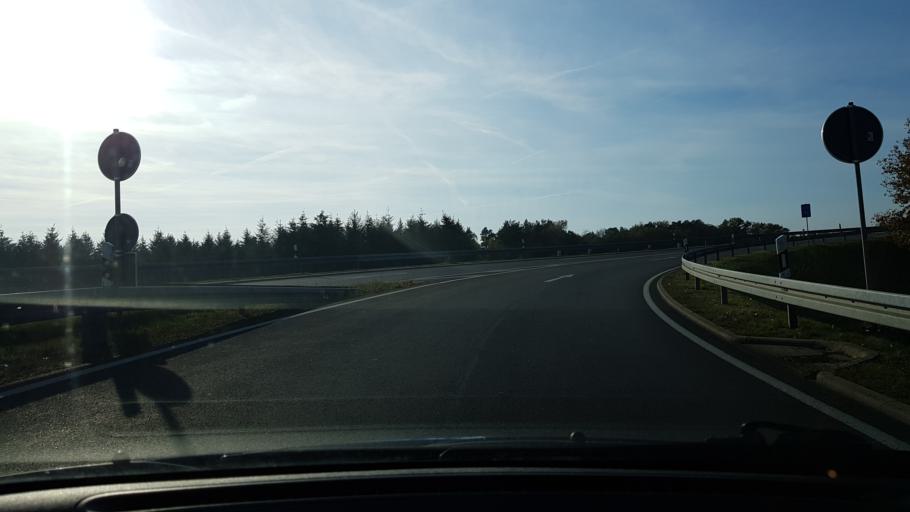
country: DE
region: Mecklenburg-Vorpommern
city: Stralendorf
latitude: 53.4846
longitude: 11.2719
